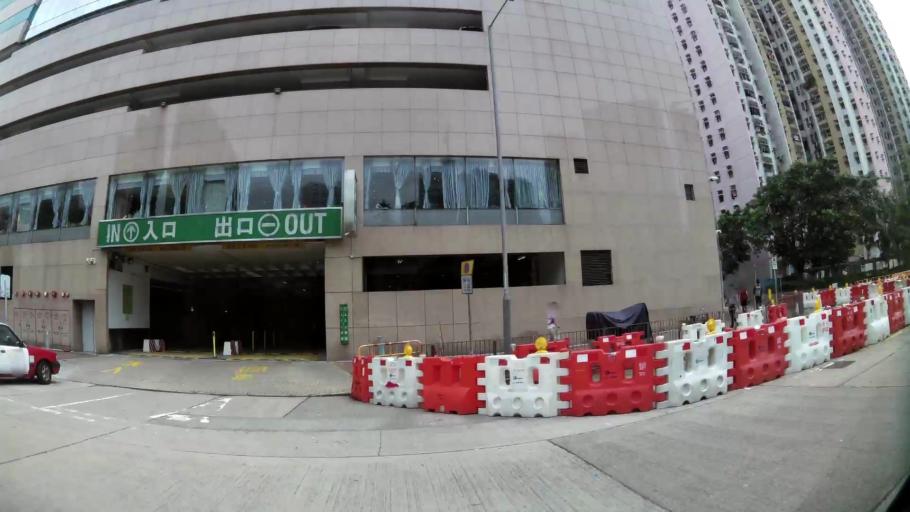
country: HK
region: Sham Shui Po
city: Sham Shui Po
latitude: 22.3371
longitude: 114.1532
